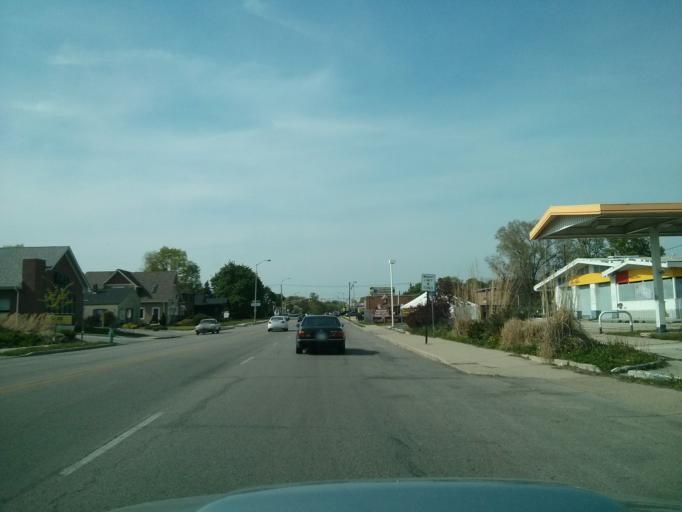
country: US
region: Indiana
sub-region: Marion County
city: Broad Ripple
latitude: 39.8705
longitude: -86.1461
